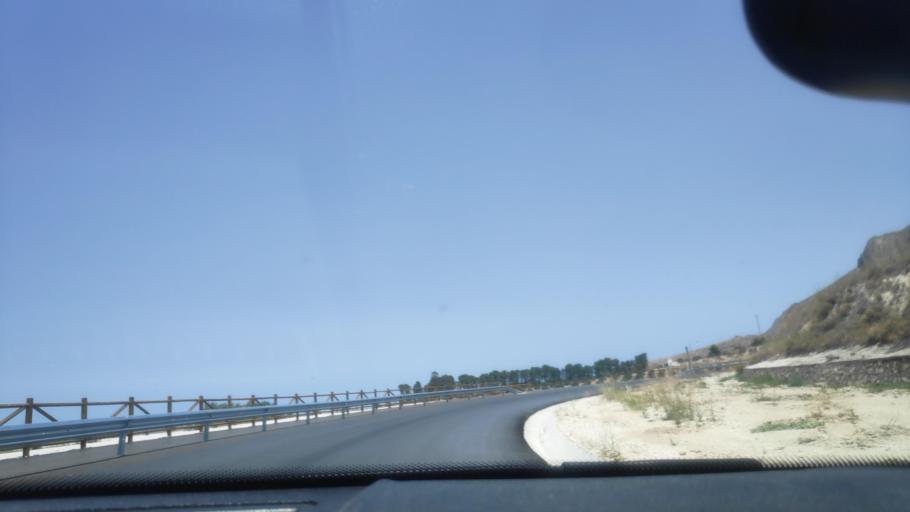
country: ES
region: Andalusia
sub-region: Provincia de Jaen
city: Jodar
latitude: 37.8091
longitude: -3.4143
